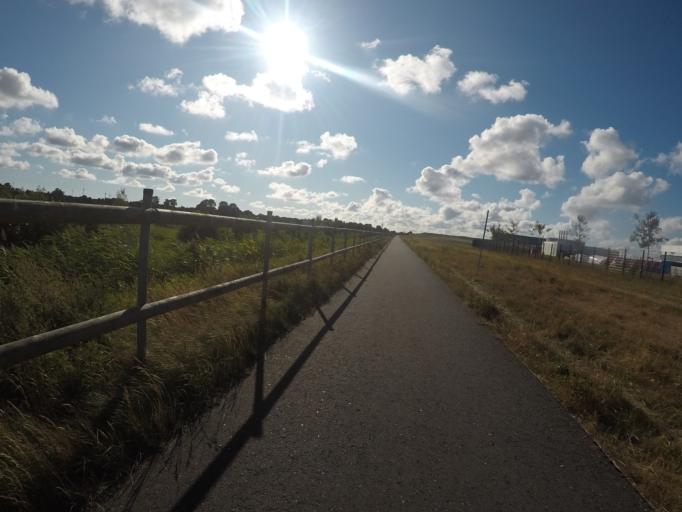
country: DE
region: Lower Saxony
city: Cuxhaven
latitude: 53.8393
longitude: 8.7527
